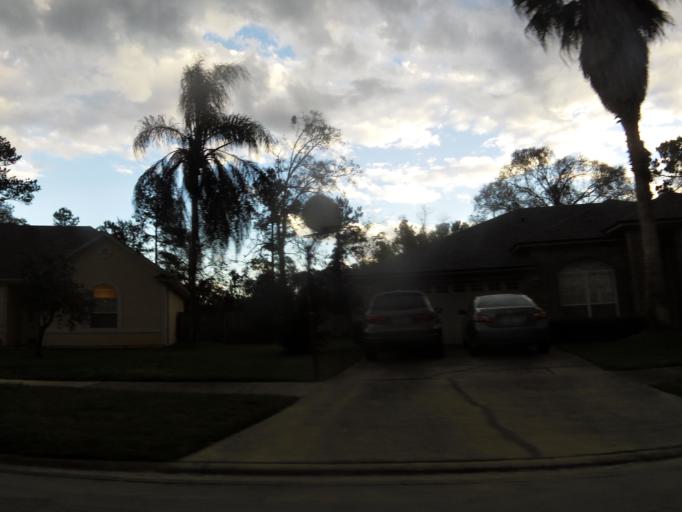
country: US
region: Florida
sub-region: Saint Johns County
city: Fruit Cove
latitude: 30.1801
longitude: -81.5677
